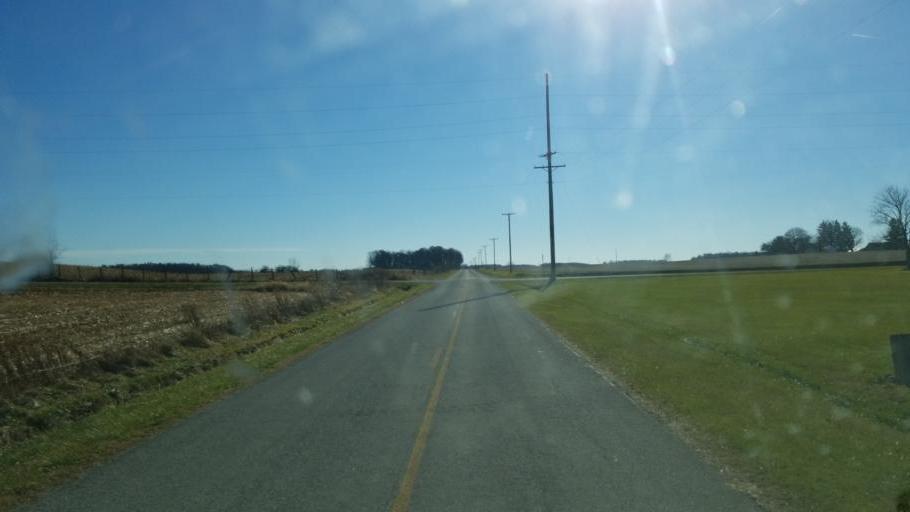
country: US
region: Ohio
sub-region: Crawford County
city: Crestline
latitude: 40.8367
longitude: -82.8374
